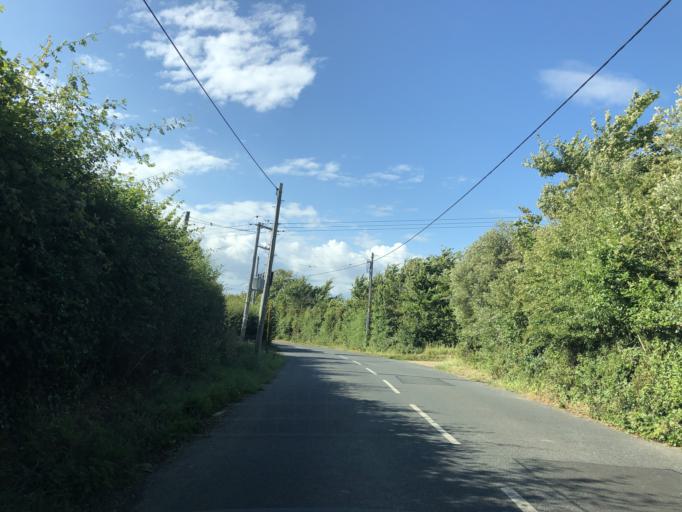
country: GB
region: England
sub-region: Isle of Wight
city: Shalfleet
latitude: 50.6979
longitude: -1.4334
